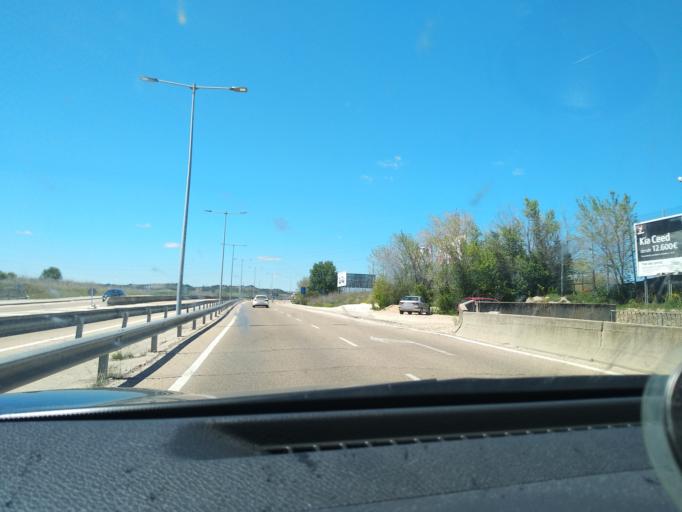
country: ES
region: Castille and Leon
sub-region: Provincia de Valladolid
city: Zaratan
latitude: 41.6433
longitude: -4.7631
